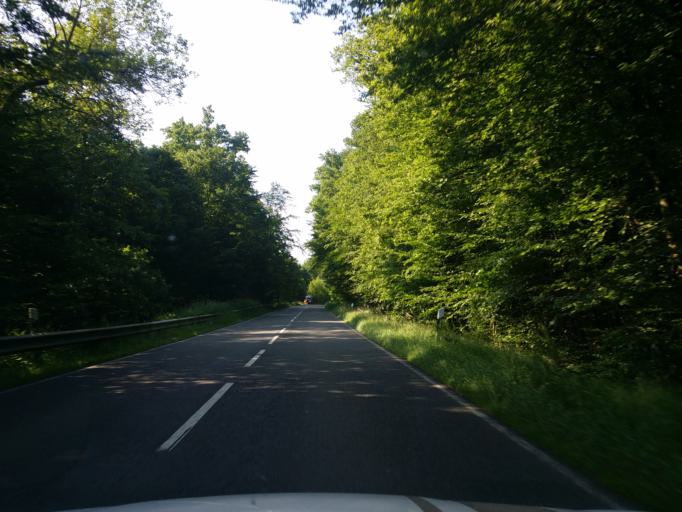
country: DE
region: Hesse
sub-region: Regierungsbezirk Darmstadt
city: Glashutten
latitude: 50.1973
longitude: 8.3524
